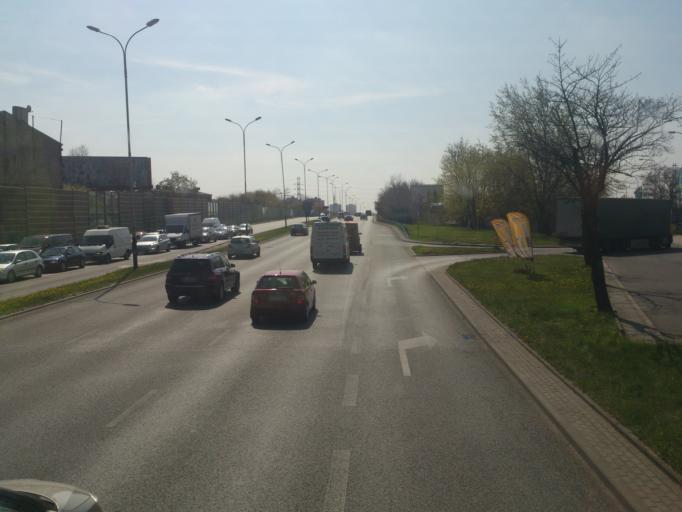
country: PL
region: Lodz Voivodeship
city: Lodz
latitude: 51.7444
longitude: 19.4406
